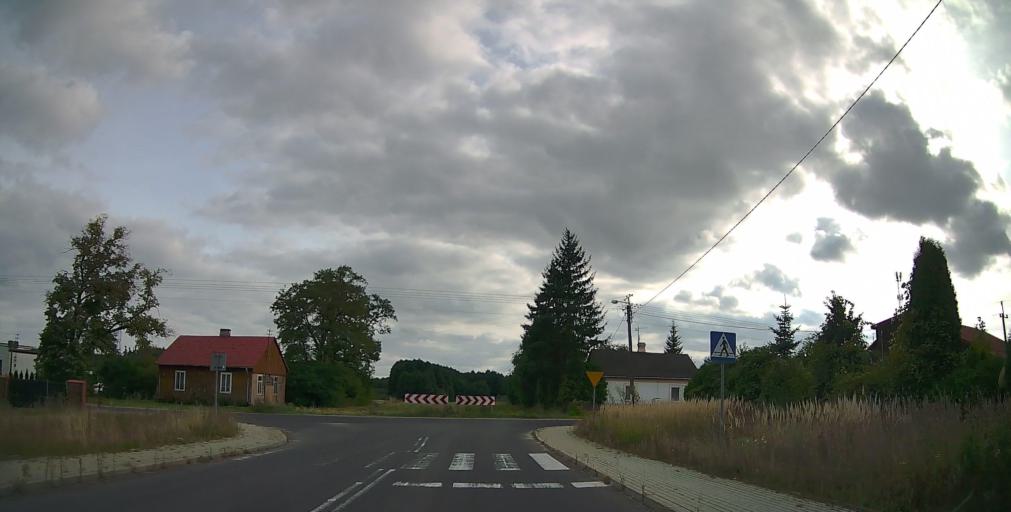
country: PL
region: Masovian Voivodeship
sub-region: Powiat grojecki
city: Goszczyn
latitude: 51.7344
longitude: 20.9123
